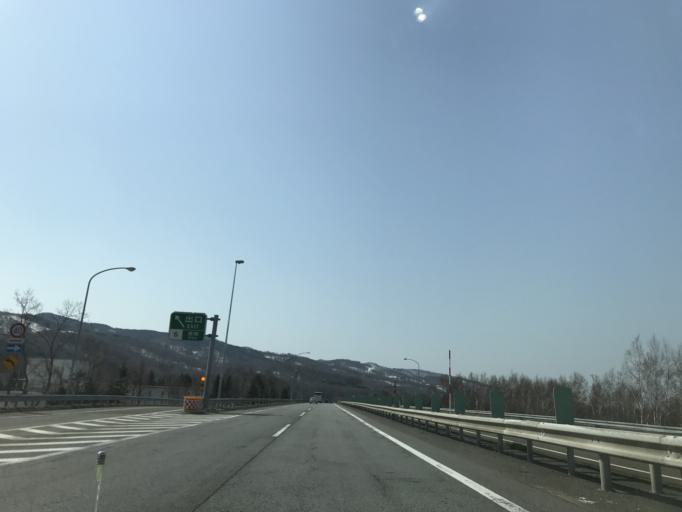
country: JP
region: Hokkaido
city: Bibai
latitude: 43.3348
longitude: 141.8883
